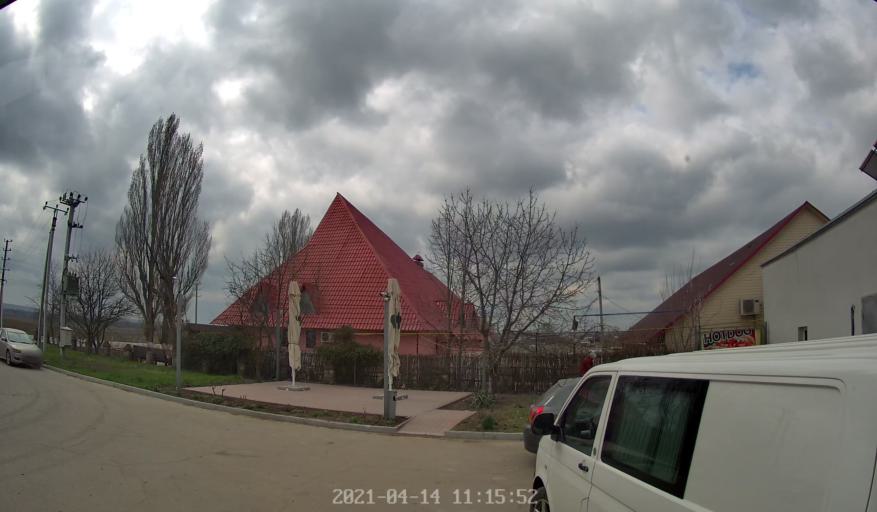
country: MD
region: Criuleni
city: Criuleni
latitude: 47.1526
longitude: 29.1531
